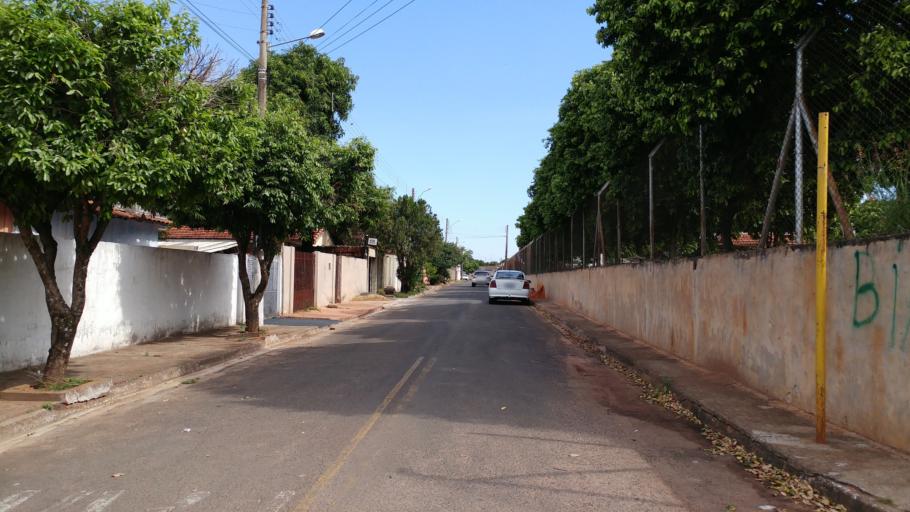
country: BR
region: Sao Paulo
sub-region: Paraguacu Paulista
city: Paraguacu Paulista
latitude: -22.4093
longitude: -50.5804
